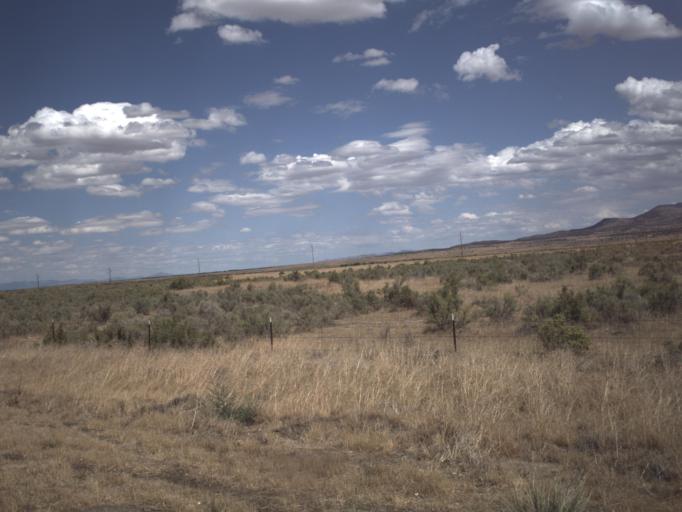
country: US
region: Utah
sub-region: Millard County
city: Delta
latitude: 39.2372
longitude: -112.4310
